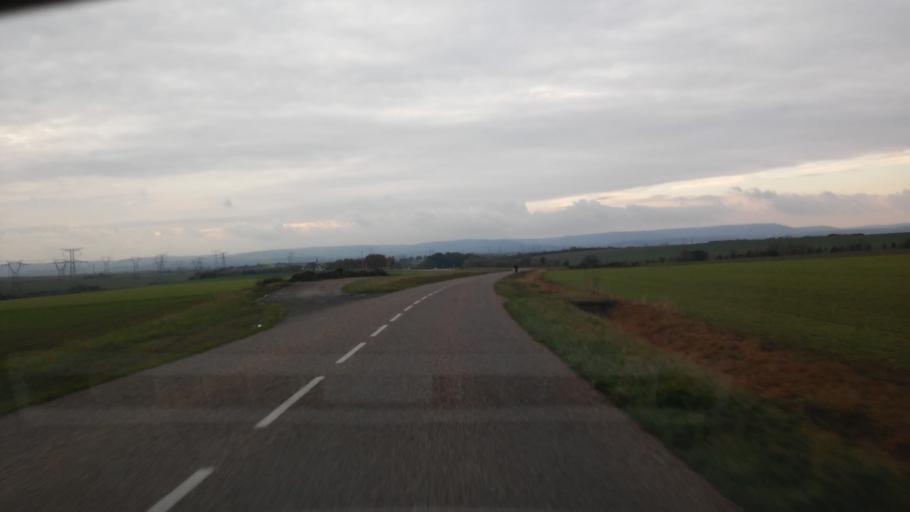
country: FR
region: Lorraine
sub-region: Departement de la Moselle
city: Vigy
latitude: 49.1983
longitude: 6.2695
